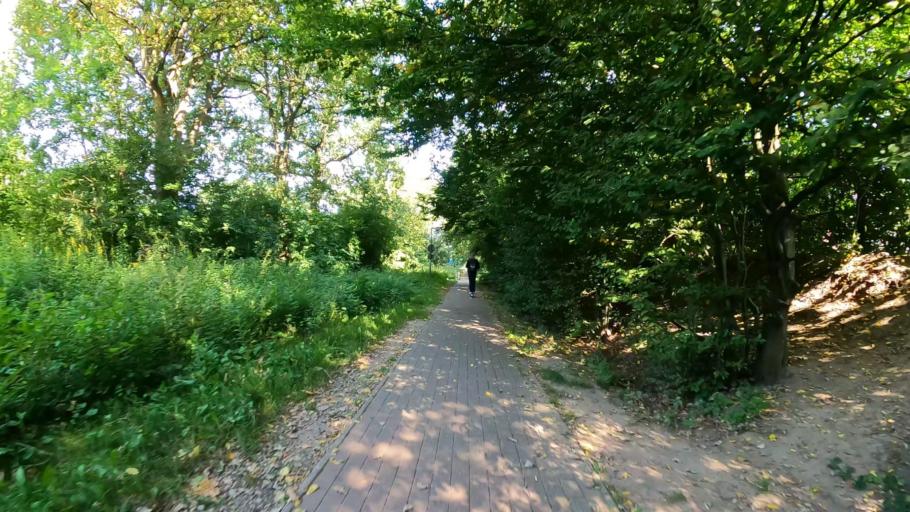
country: DE
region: Schleswig-Holstein
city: Henstedt-Ulzburg
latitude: 53.7776
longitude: 9.9753
